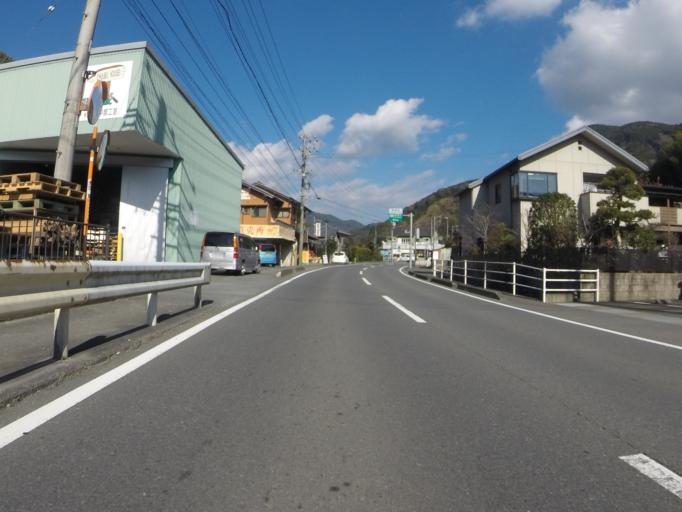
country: JP
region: Shizuoka
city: Fujinomiya
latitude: 35.1072
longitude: 138.5131
